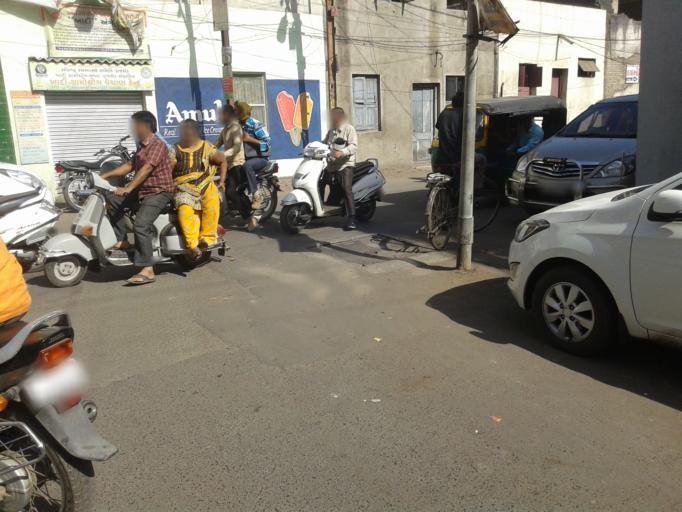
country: IN
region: Gujarat
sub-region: Rajkot
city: Rajkot
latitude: 22.2887
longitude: 70.7970
